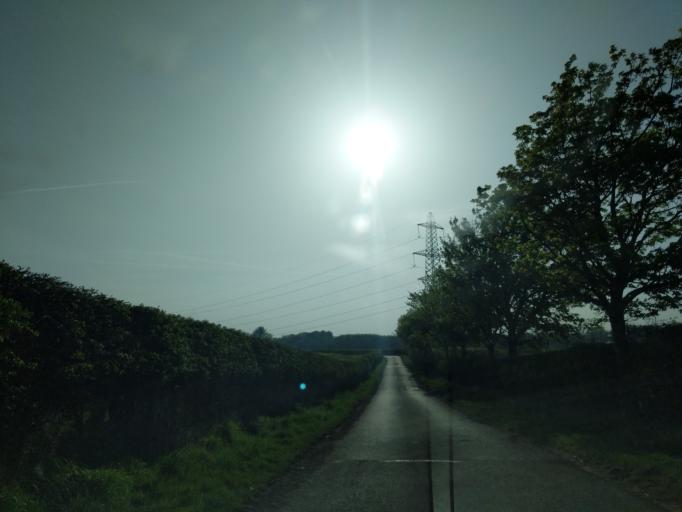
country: GB
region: Scotland
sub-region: Fife
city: Pathhead
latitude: 55.8567
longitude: -2.9357
